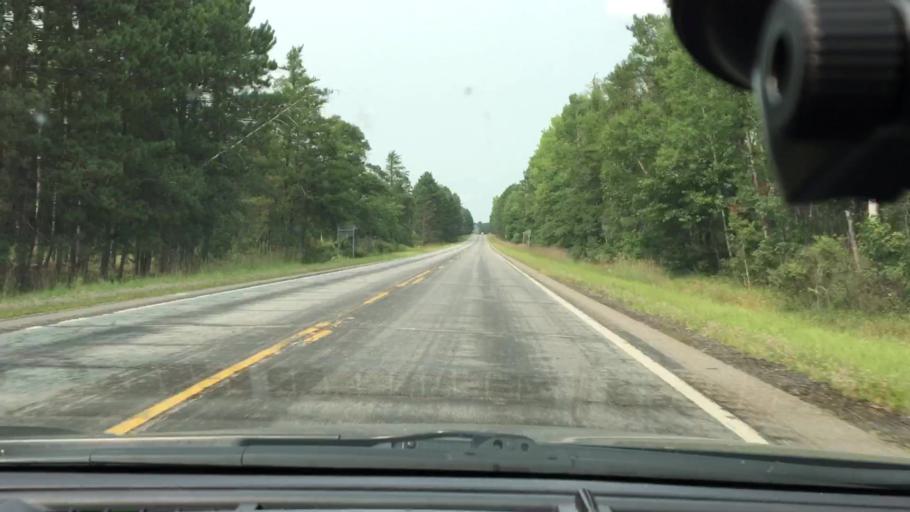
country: US
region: Minnesota
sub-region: Crow Wing County
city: Cross Lake
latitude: 46.7448
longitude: -93.9669
